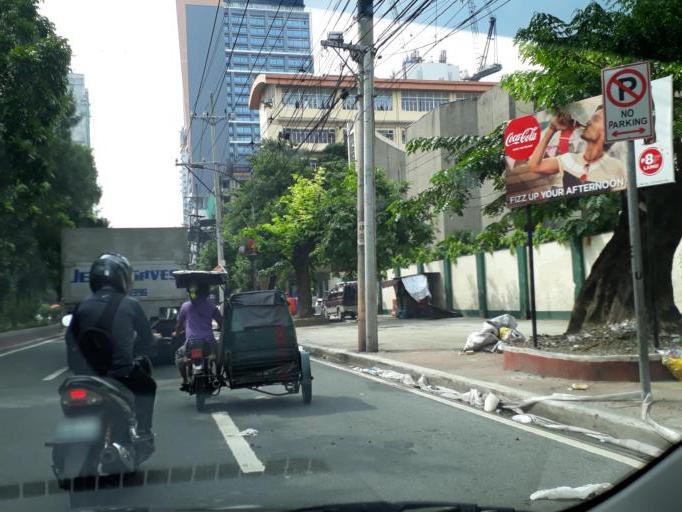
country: PH
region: Metro Manila
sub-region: City of Manila
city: Manila
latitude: 14.6109
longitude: 120.9914
